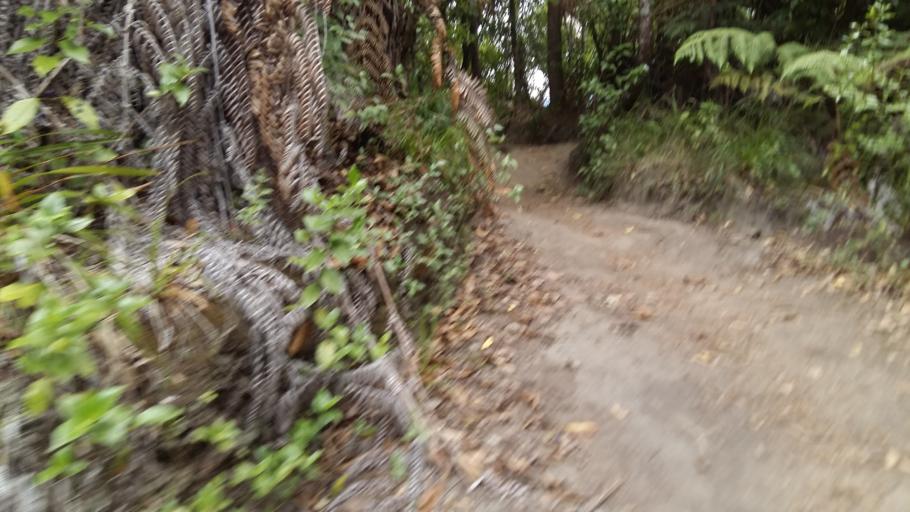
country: NZ
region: Bay of Plenty
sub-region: Whakatane District
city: Whakatane
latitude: -37.9532
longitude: 177.0036
